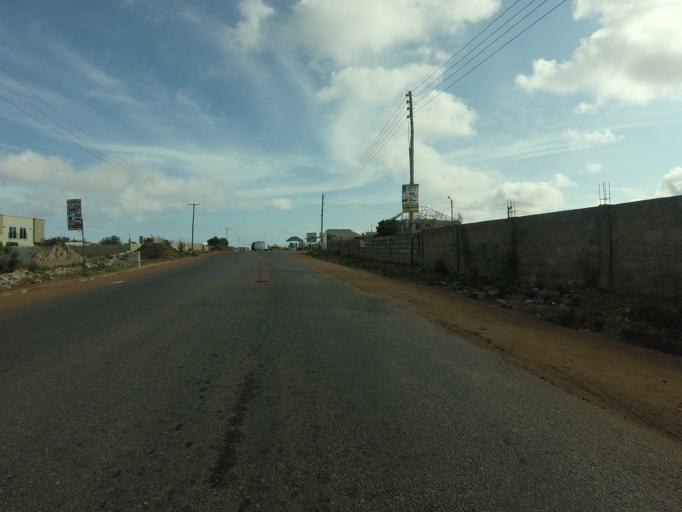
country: GH
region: Greater Accra
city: Teshi Old Town
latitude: 5.5953
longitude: -0.1363
